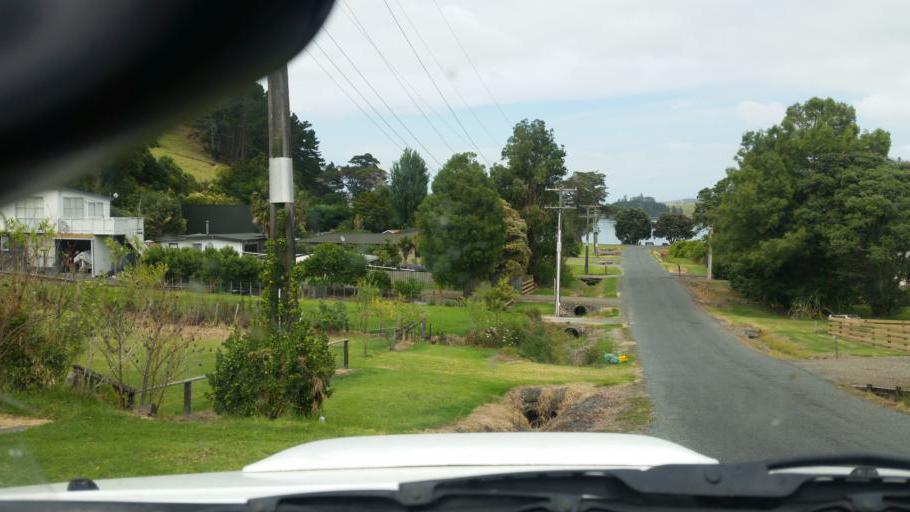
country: NZ
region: Auckland
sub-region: Auckland
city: Wellsford
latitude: -36.1578
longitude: 174.2390
